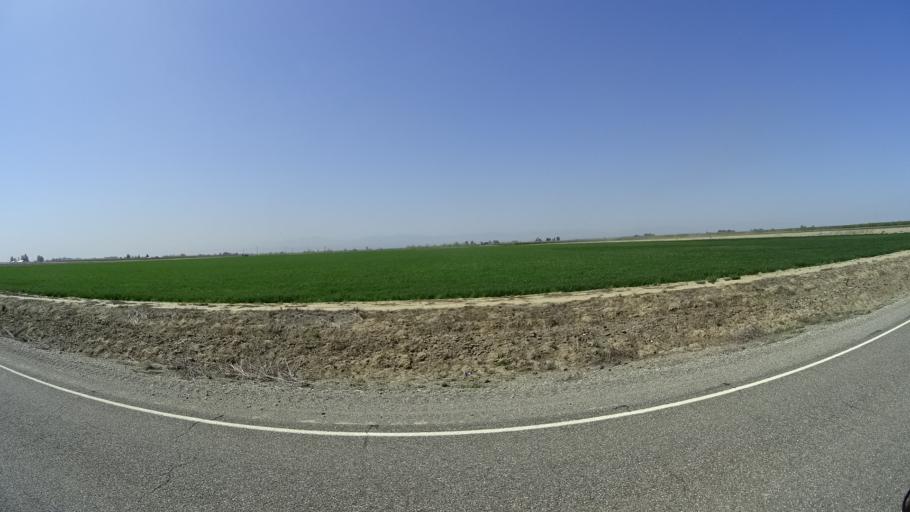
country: US
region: California
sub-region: Glenn County
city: Willows
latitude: 39.5667
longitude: -122.1370
